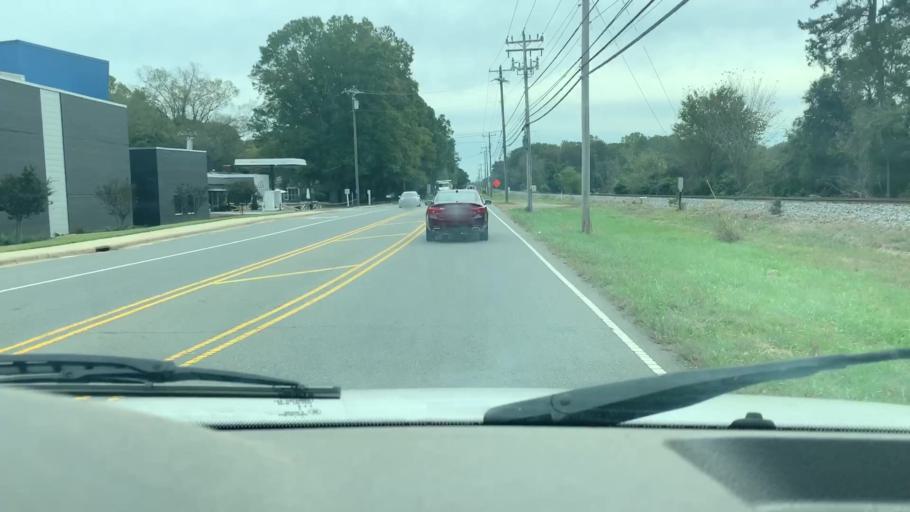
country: US
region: North Carolina
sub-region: Gaston County
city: Davidson
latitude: 35.5350
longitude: -80.8469
